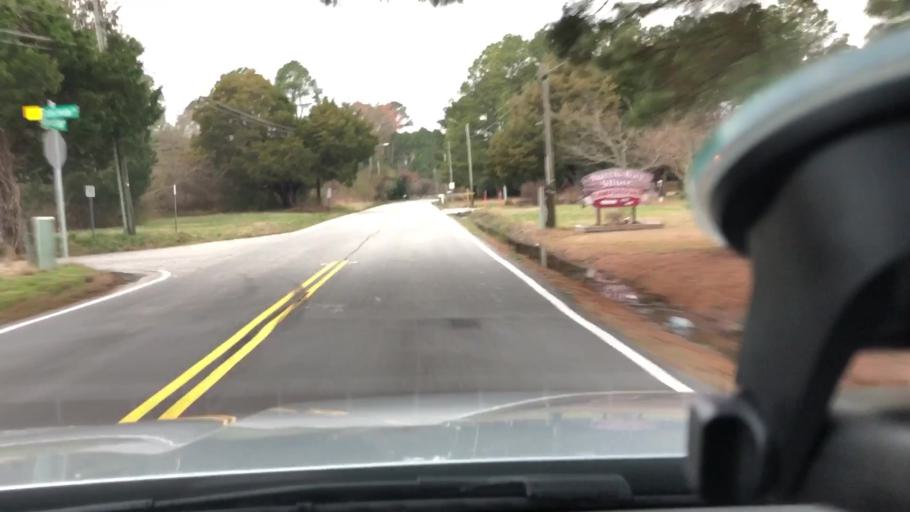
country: US
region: Virginia
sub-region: City of Virginia Beach
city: Virginia Beach
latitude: 36.7306
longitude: -75.9790
